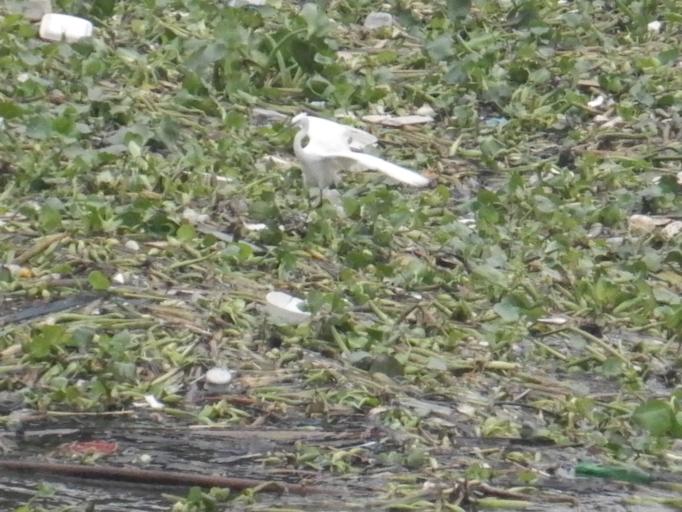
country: TH
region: Bangkok
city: Bangkok
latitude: 13.7430
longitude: 100.4910
